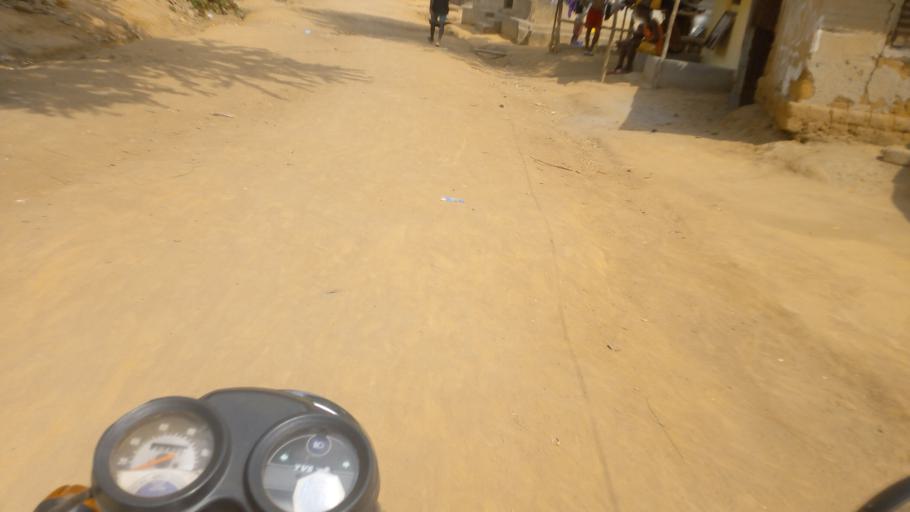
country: SL
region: Western Area
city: Waterloo
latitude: 8.3234
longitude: -13.0619
